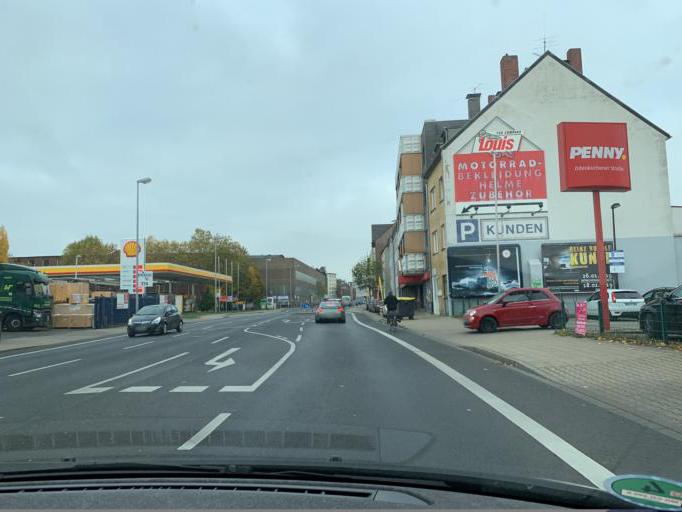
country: DE
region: North Rhine-Westphalia
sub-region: Regierungsbezirk Dusseldorf
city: Monchengladbach
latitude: 51.1583
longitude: 6.4471
